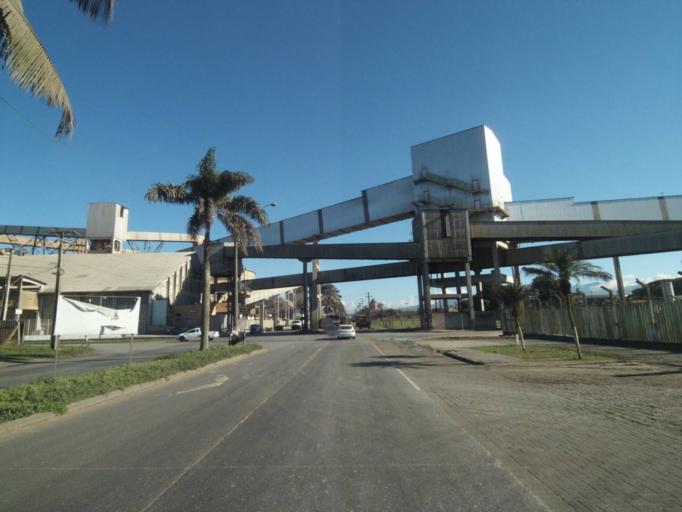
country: BR
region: Parana
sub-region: Paranagua
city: Paranagua
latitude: -25.5075
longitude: -48.5144
